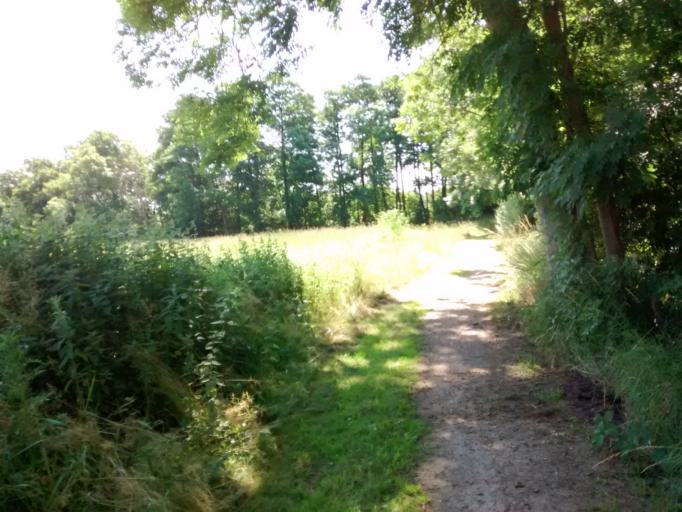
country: DK
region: Zealand
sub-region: Soro Kommune
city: Soro
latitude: 55.4531
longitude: 11.5848
